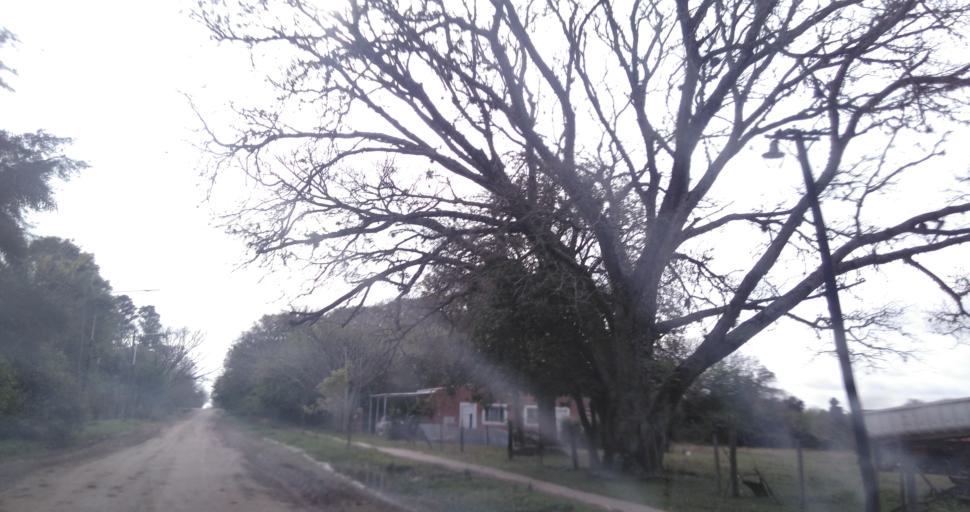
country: AR
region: Chaco
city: Colonia Benitez
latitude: -27.3314
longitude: -58.9523
